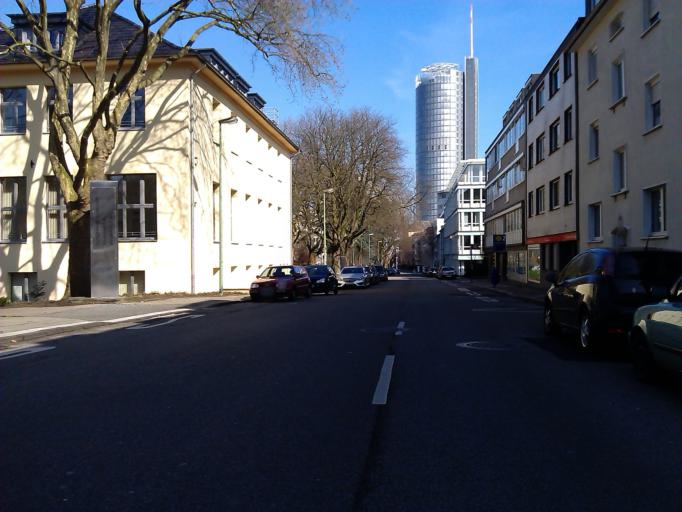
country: DE
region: North Rhine-Westphalia
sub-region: Regierungsbezirk Dusseldorf
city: Essen
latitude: 51.4440
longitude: 7.0130
